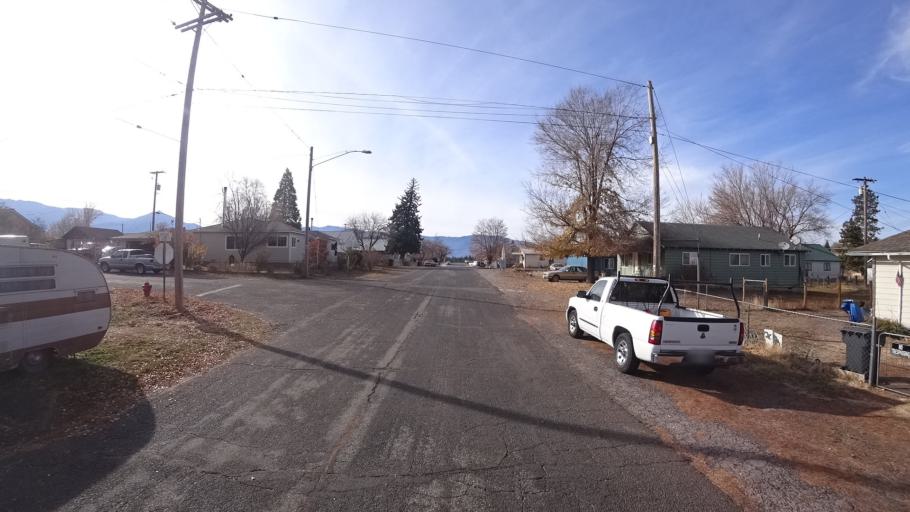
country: US
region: California
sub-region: Siskiyou County
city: Weed
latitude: 41.4385
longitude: -122.3780
